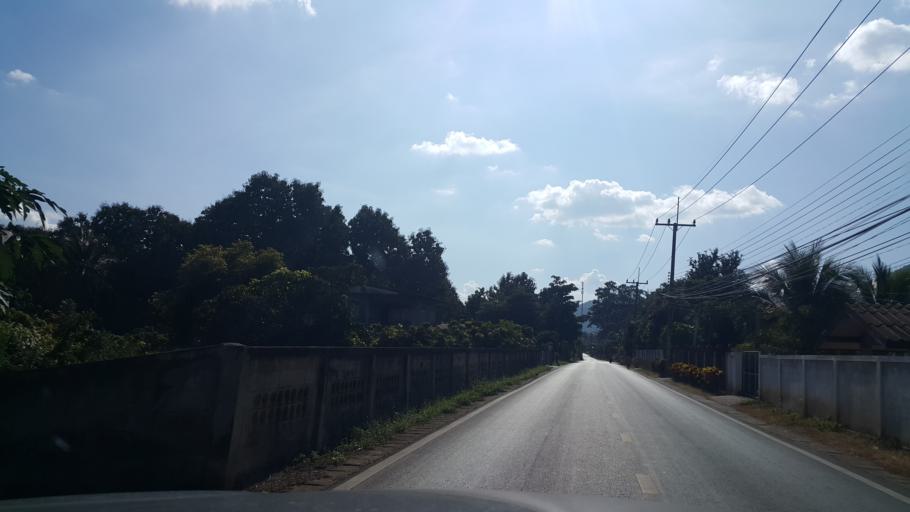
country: TH
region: Lamphun
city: Mae Tha
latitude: 18.5179
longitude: 99.2202
